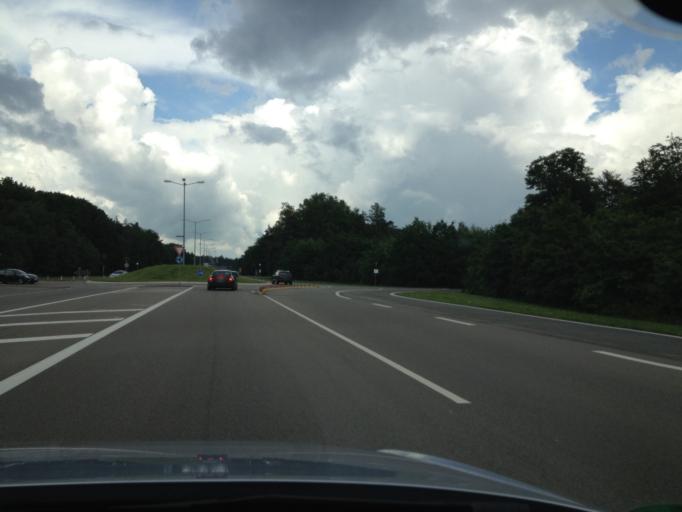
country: DE
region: Rheinland-Pfalz
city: Ramstein-Miesenbach
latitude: 49.4378
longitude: 7.5671
